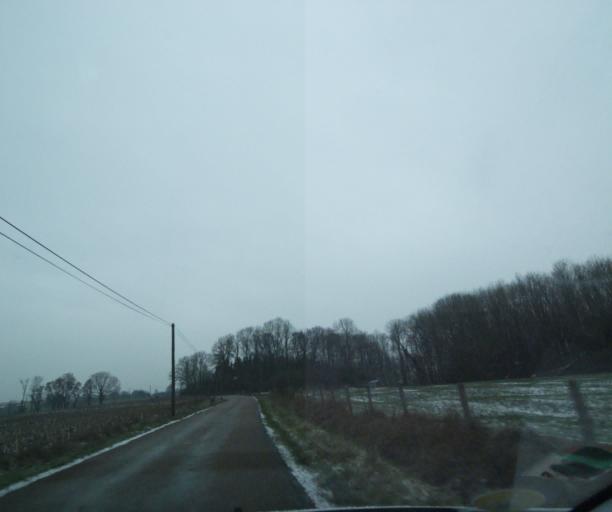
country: FR
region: Champagne-Ardenne
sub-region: Departement de la Haute-Marne
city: Wassy
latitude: 48.4667
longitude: 5.0357
